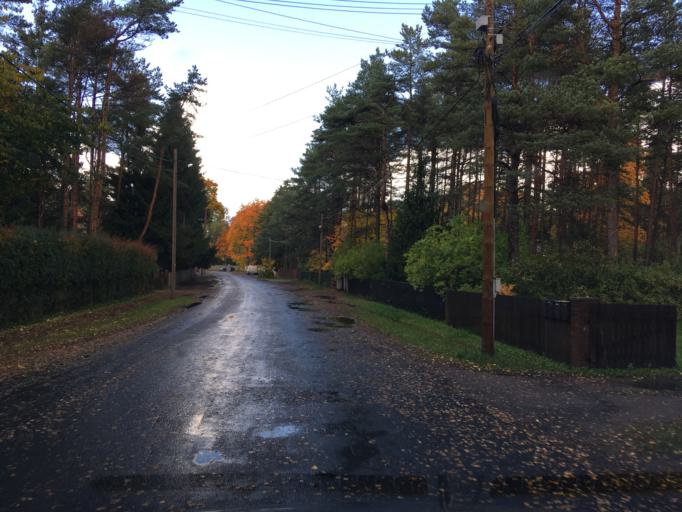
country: EE
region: Harju
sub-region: Tallinna linn
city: Tallinn
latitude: 59.3816
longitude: 24.7066
